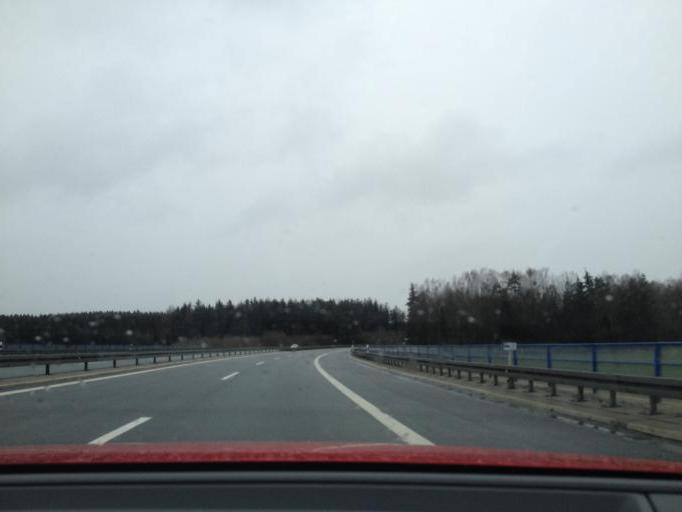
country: DE
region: Bavaria
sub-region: Upper Franconia
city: Schonwald
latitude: 50.2054
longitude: 12.1089
